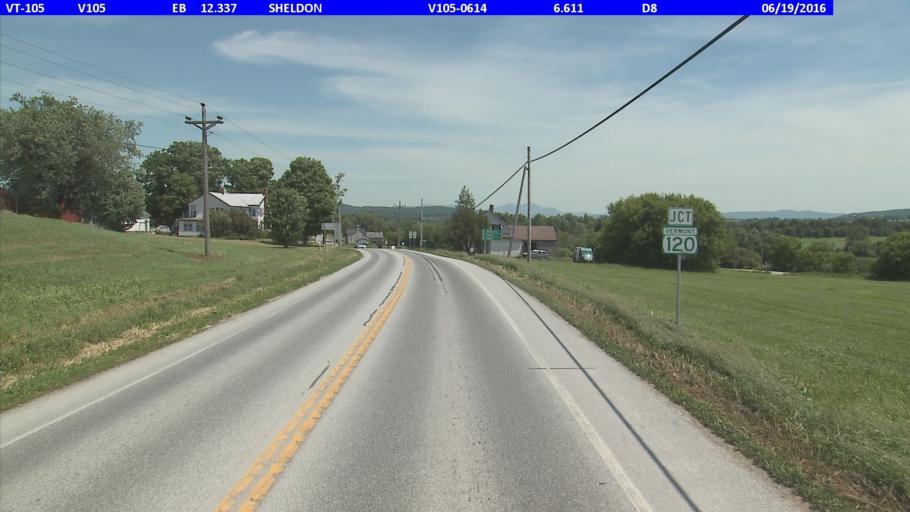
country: US
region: Vermont
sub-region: Franklin County
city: Enosburg Falls
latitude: 44.9100
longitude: -72.9068
